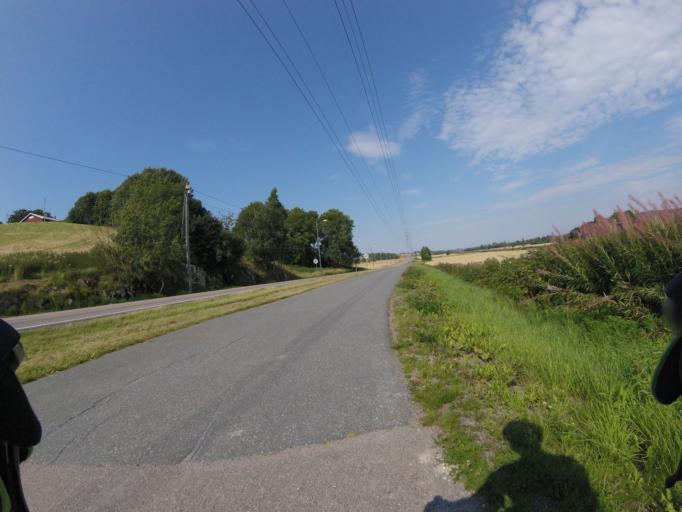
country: NO
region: Akershus
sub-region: Skedsmo
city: Lillestrom
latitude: 59.9723
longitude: 11.0673
